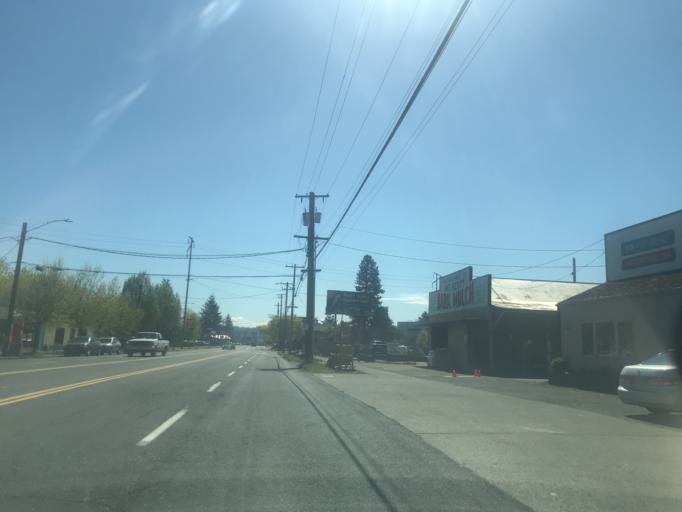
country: US
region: Oregon
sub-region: Multnomah County
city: Lents
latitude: 45.4879
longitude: -122.5928
